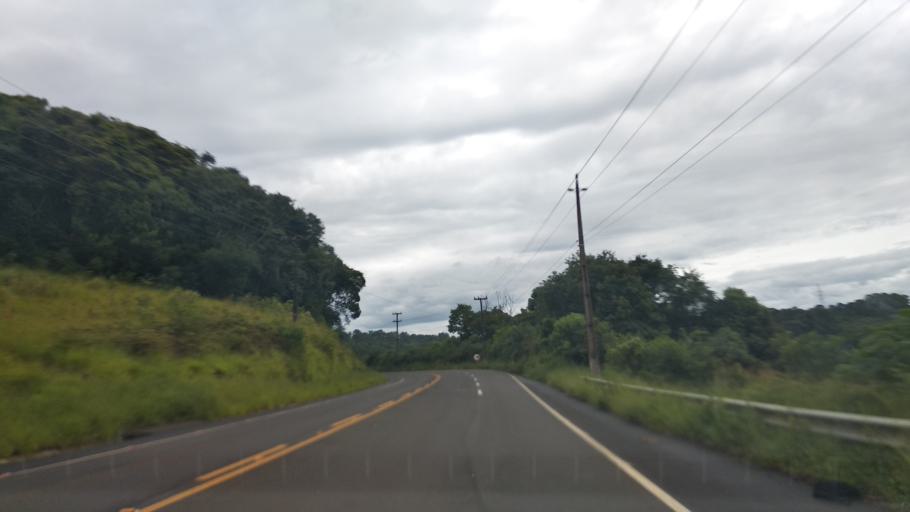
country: BR
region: Santa Catarina
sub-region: Videira
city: Videira
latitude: -27.0491
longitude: -51.1694
